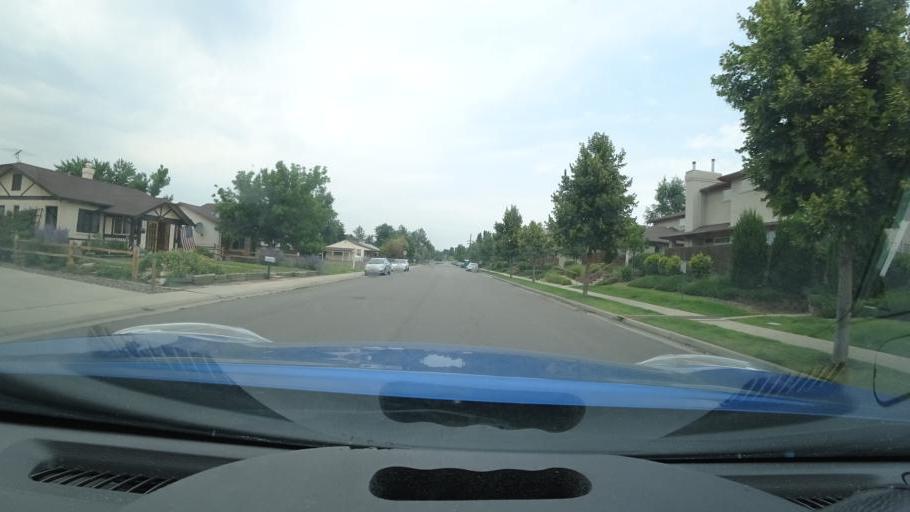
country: US
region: Colorado
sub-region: Arapahoe County
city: Glendale
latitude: 39.6991
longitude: -104.9141
